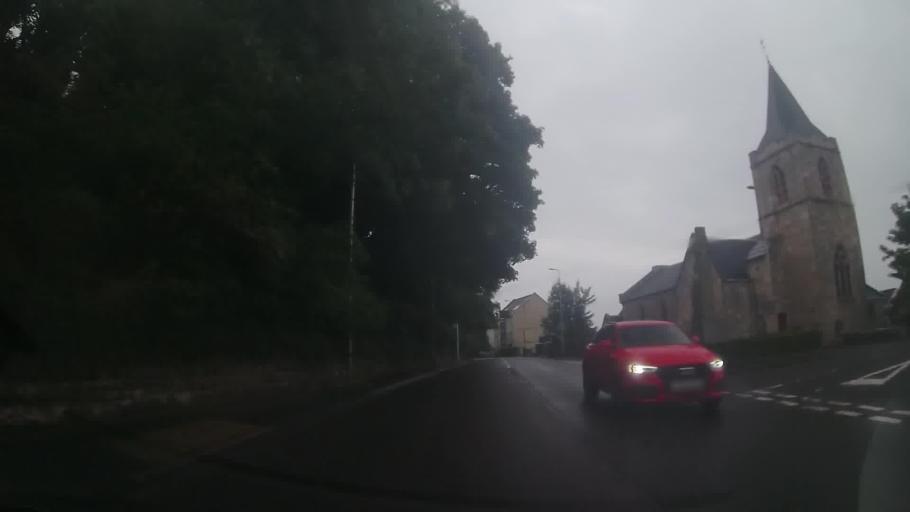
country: GB
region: Scotland
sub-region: North Ayrshire
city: Fairlie
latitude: 55.7608
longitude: -4.8540
